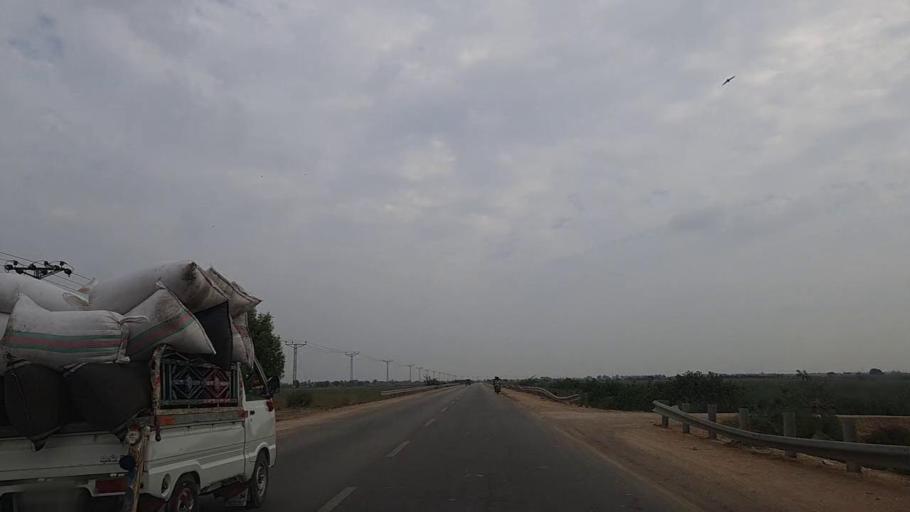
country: PK
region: Sindh
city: Thatta
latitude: 24.6168
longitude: 68.0667
